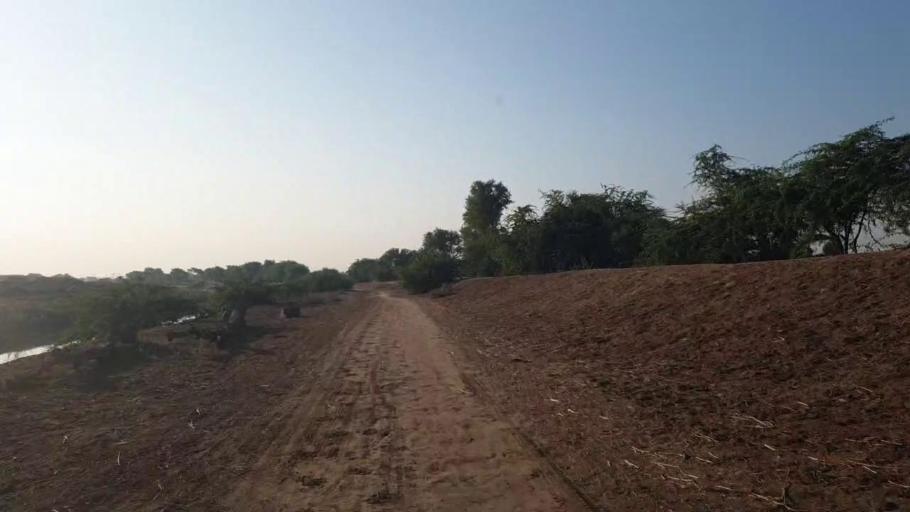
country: PK
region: Sindh
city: Badin
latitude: 24.6389
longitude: 68.7917
